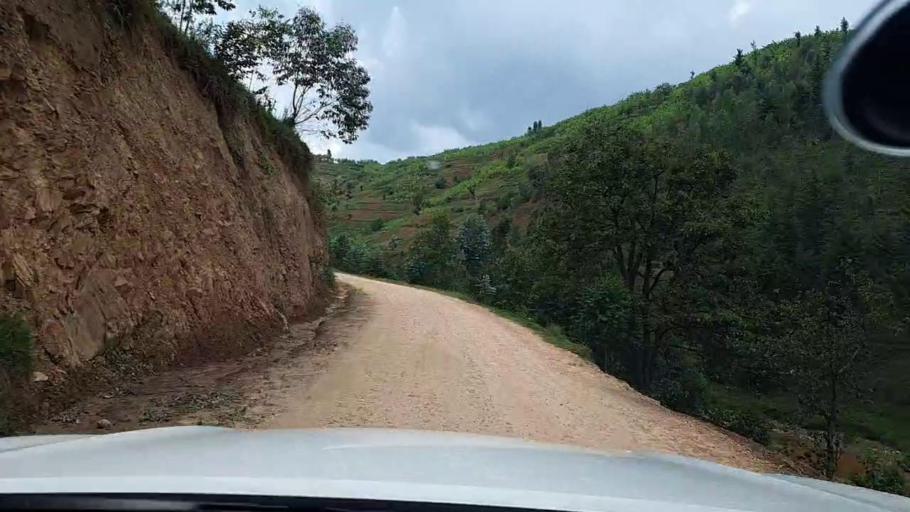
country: RW
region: Western Province
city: Kibuye
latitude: -2.1260
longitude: 29.4266
